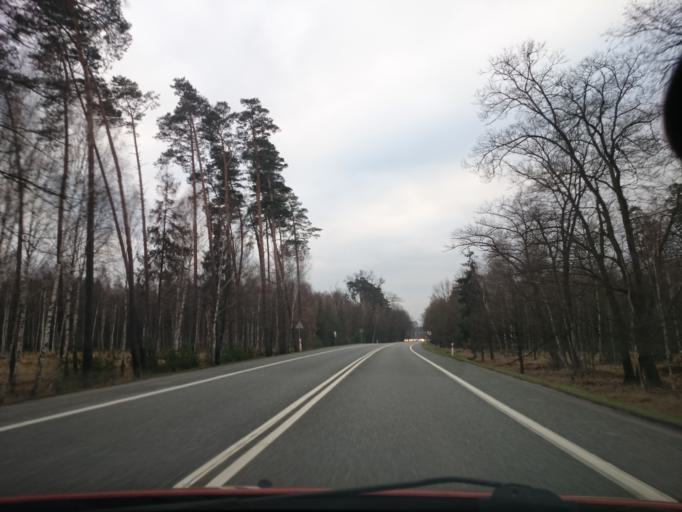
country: PL
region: Opole Voivodeship
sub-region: Powiat opolski
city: Dabrowa
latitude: 50.6715
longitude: 17.7051
